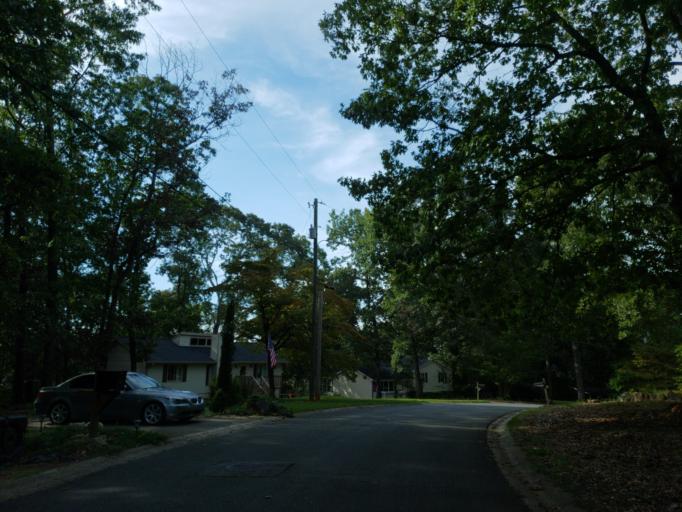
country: US
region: Georgia
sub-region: Cherokee County
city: Woodstock
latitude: 34.0438
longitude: -84.4841
